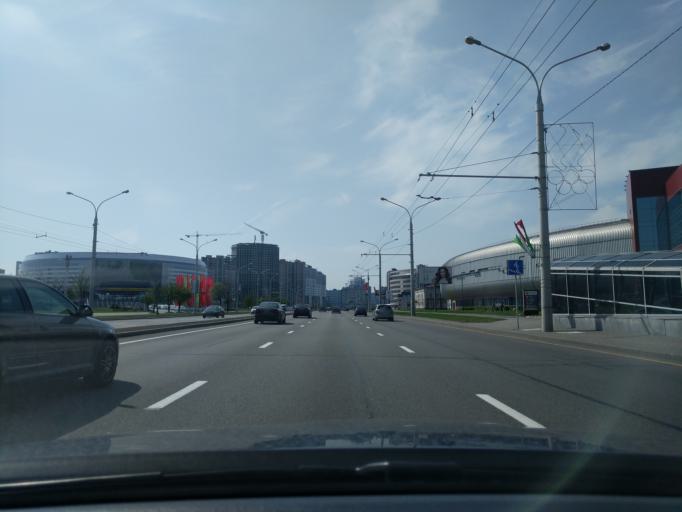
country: BY
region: Minsk
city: Zhdanovichy
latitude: 53.9375
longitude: 27.4877
